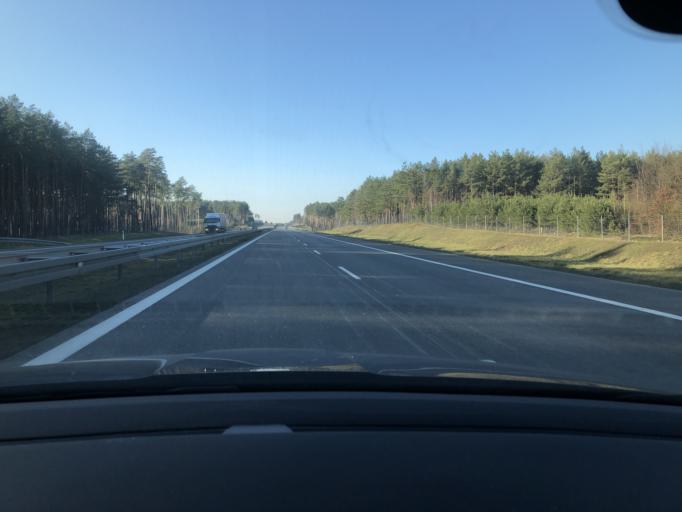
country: PL
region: Lubusz
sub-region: Powiat sulecinski
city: Torzym
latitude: 52.3264
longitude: 15.0517
